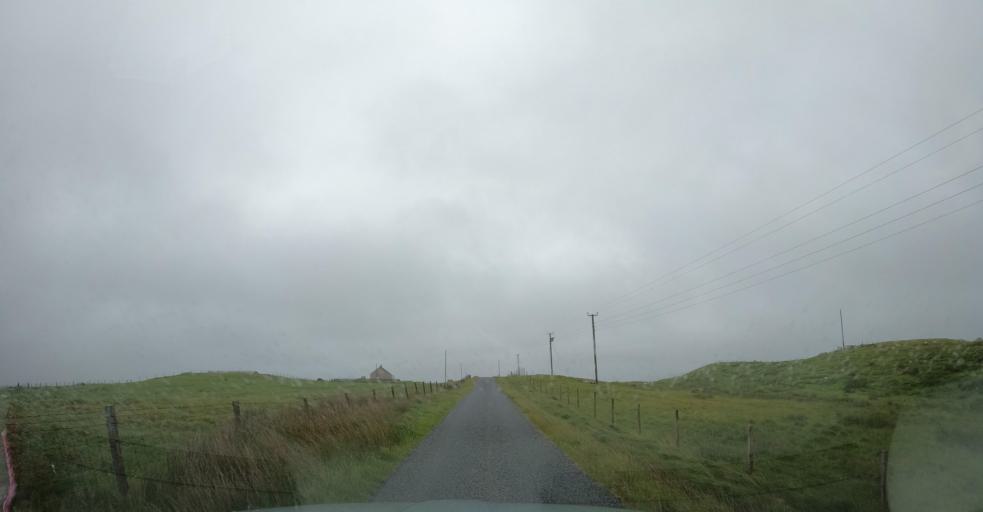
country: GB
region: Scotland
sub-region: Eilean Siar
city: Isle of North Uist
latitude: 57.5500
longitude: -7.2335
